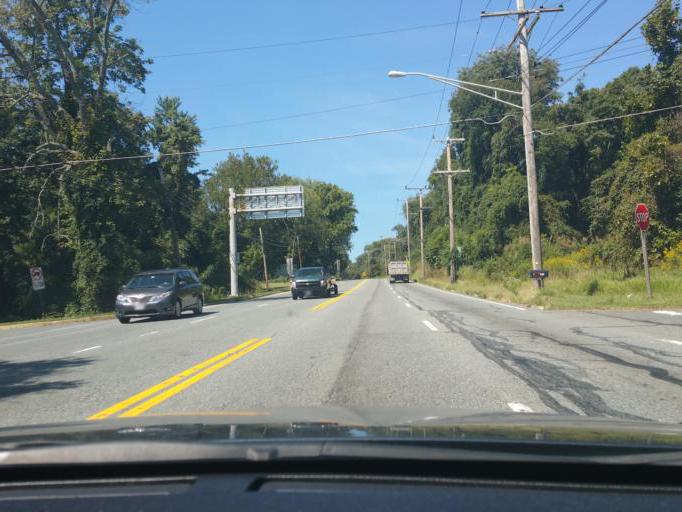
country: US
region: Maryland
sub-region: Harford County
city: Havre de Grace
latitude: 39.5596
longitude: -76.1045
